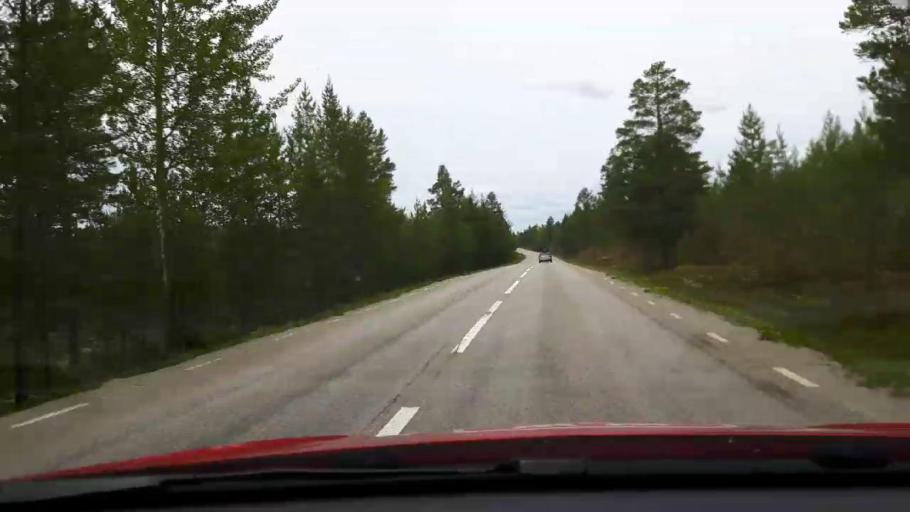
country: SE
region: Jaemtland
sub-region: Harjedalens Kommun
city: Sveg
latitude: 62.2350
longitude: 13.8536
